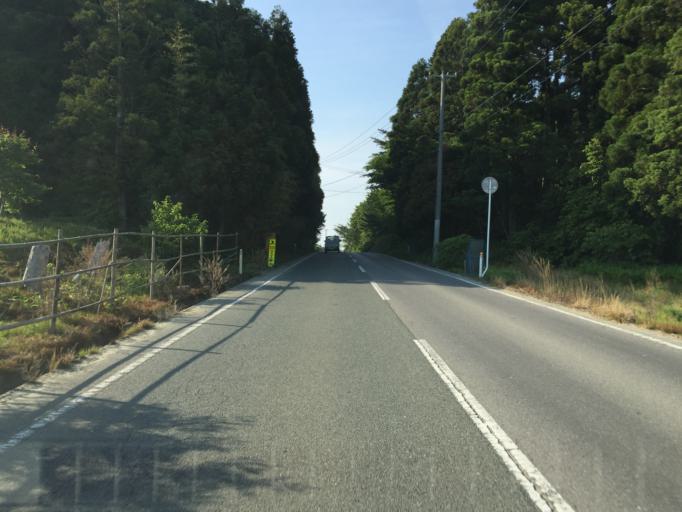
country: JP
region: Fukushima
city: Namie
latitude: 37.7415
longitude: 141.0052
